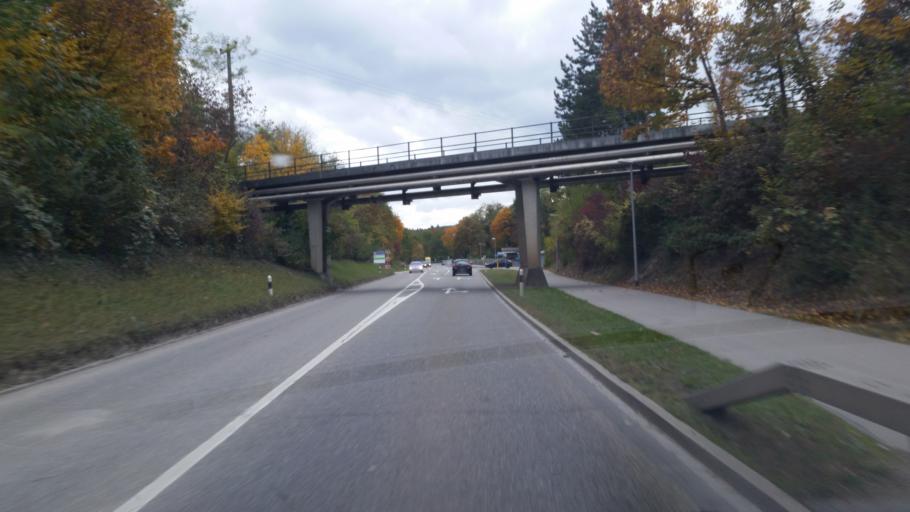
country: CH
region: Aargau
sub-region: Bezirk Brugg
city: Lauffohr (Brugg)
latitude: 47.5155
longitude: 8.2389
